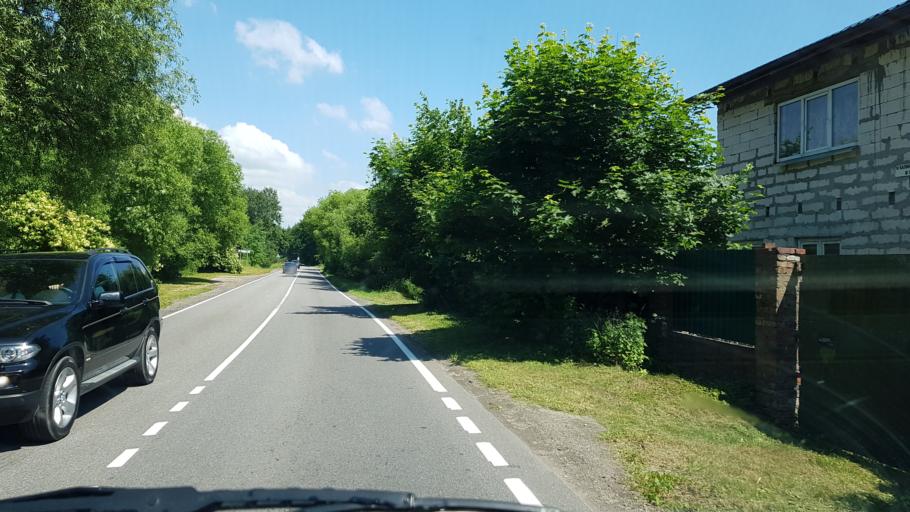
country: RU
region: Kaliningrad
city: Primorsk
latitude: 54.7284
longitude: 20.0124
